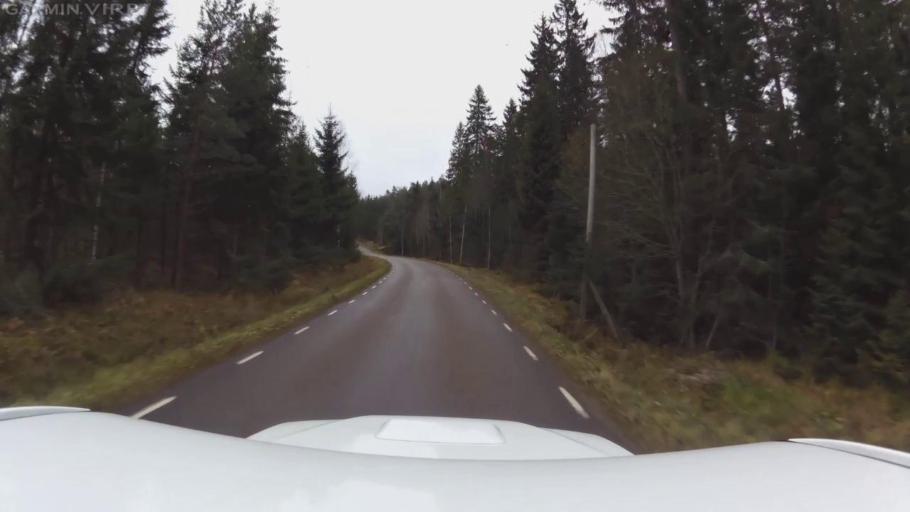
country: SE
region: OEstergoetland
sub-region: Mjolby Kommun
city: Mantorp
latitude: 58.1397
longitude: 15.4071
